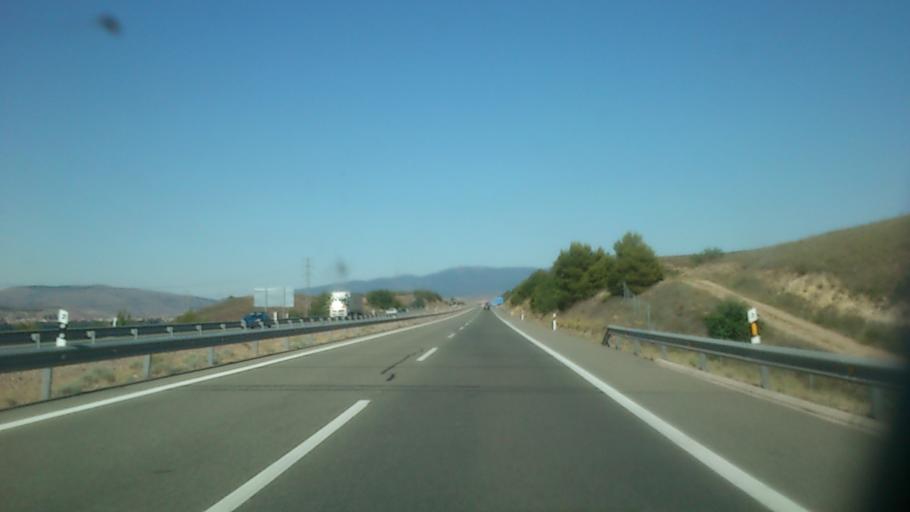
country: ES
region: Aragon
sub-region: Provincia de Zaragoza
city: Terrer
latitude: 41.3193
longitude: -1.6901
